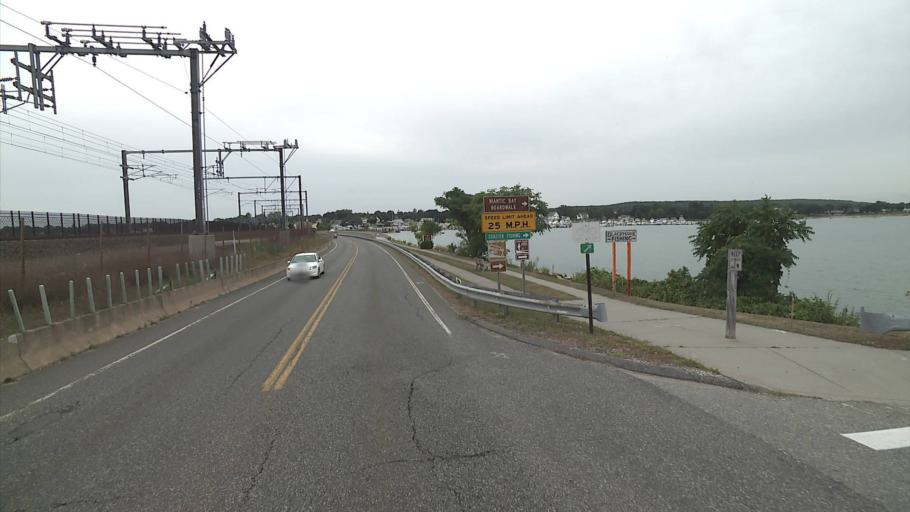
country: US
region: Connecticut
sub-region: New London County
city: Niantic
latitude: 41.3242
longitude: -72.1807
